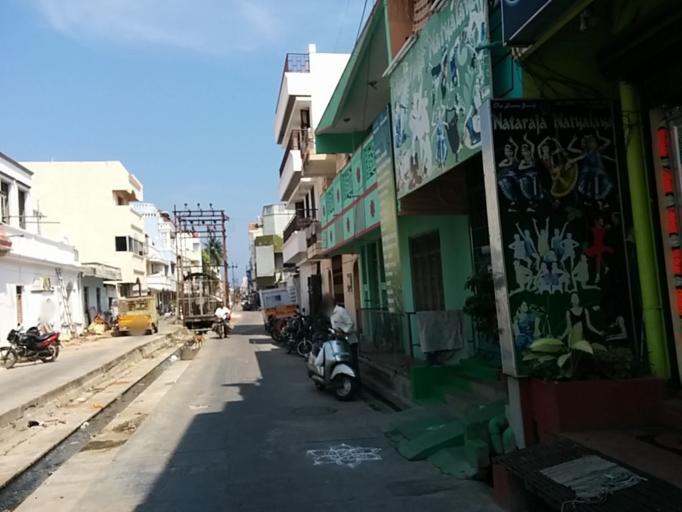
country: IN
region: Pondicherry
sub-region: Puducherry
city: Puducherry
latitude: 11.9328
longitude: 79.8247
